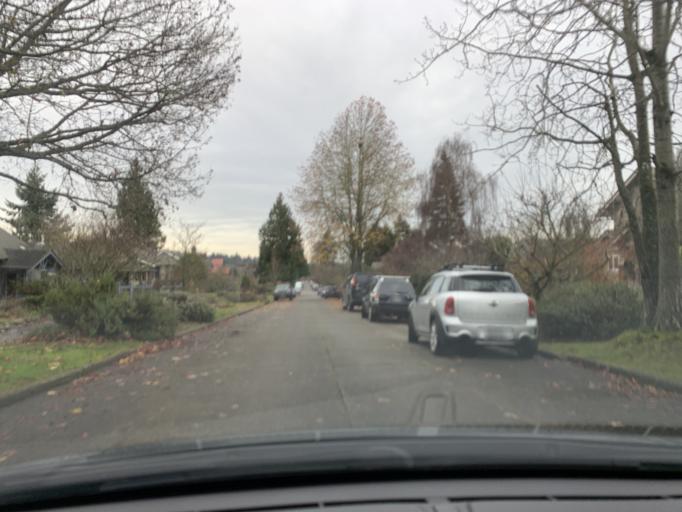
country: US
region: Washington
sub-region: King County
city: White Center
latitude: 47.5535
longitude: -122.3898
